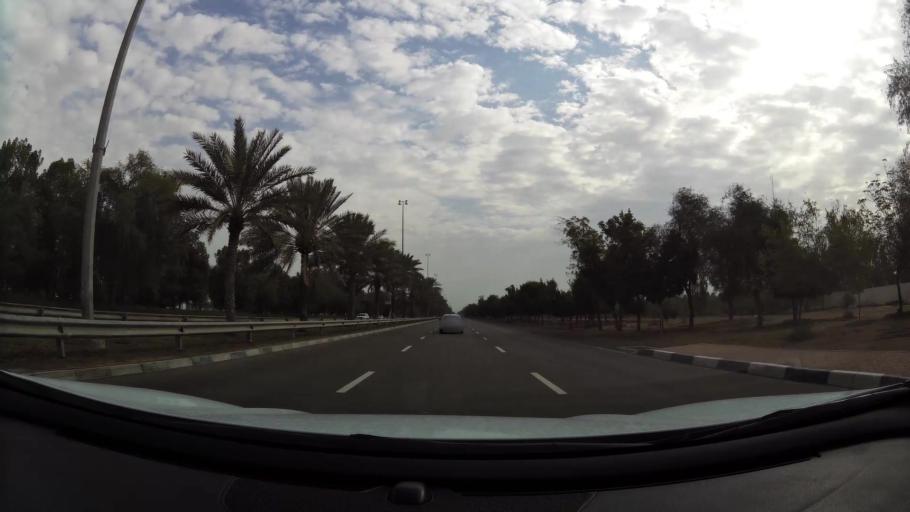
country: AE
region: Abu Dhabi
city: Al Ain
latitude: 24.1823
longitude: 55.6276
